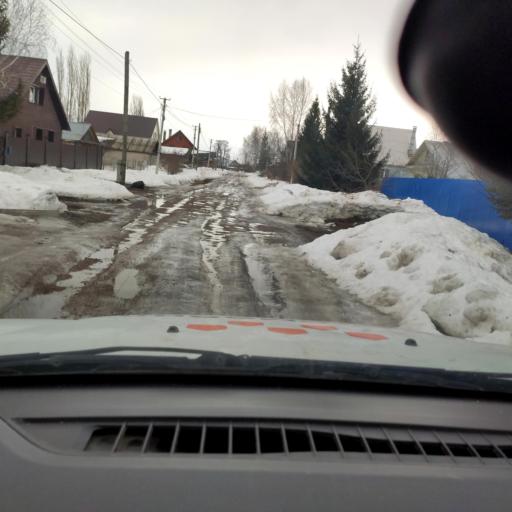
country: RU
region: Bashkortostan
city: Ufa
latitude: 54.5261
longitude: 55.9141
